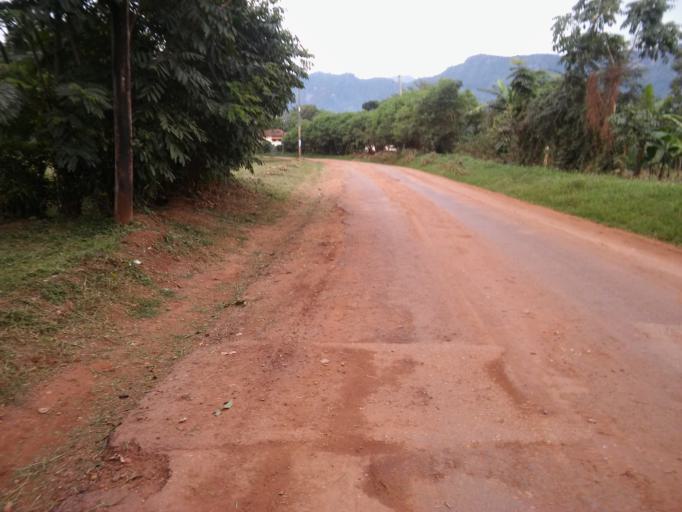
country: UG
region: Eastern Region
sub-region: Mbale District
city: Mbale
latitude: 1.0664
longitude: 34.1921
